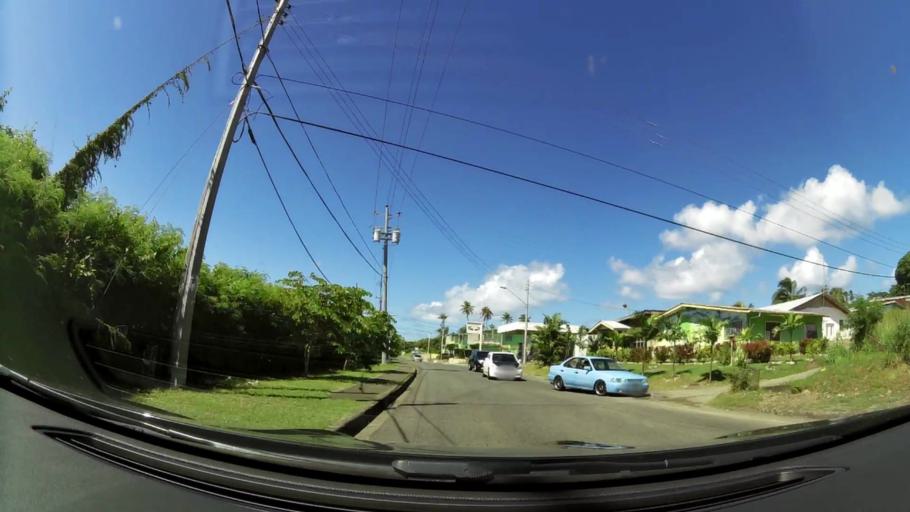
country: TT
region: Tobago
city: Scarborough
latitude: 11.1687
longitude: -60.7736
